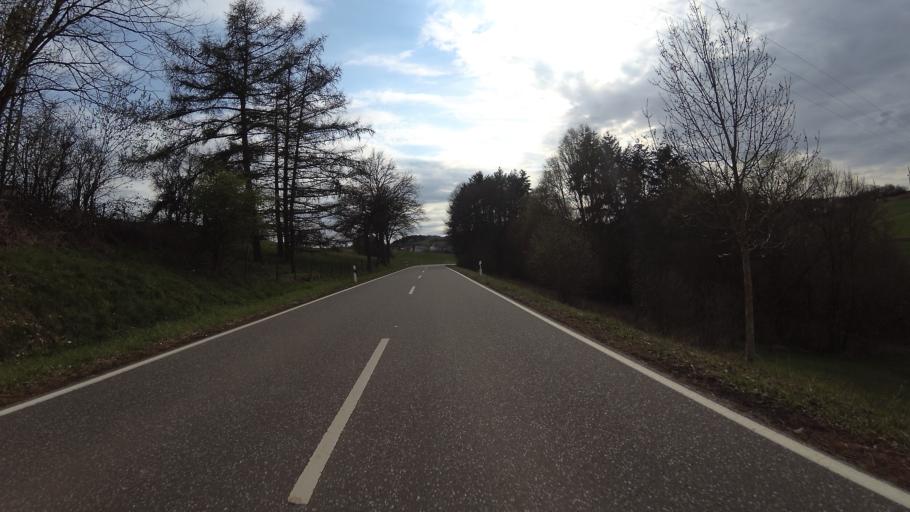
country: DE
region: Rheinland-Pfalz
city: Wahnwegen
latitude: 49.4859
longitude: 7.3860
